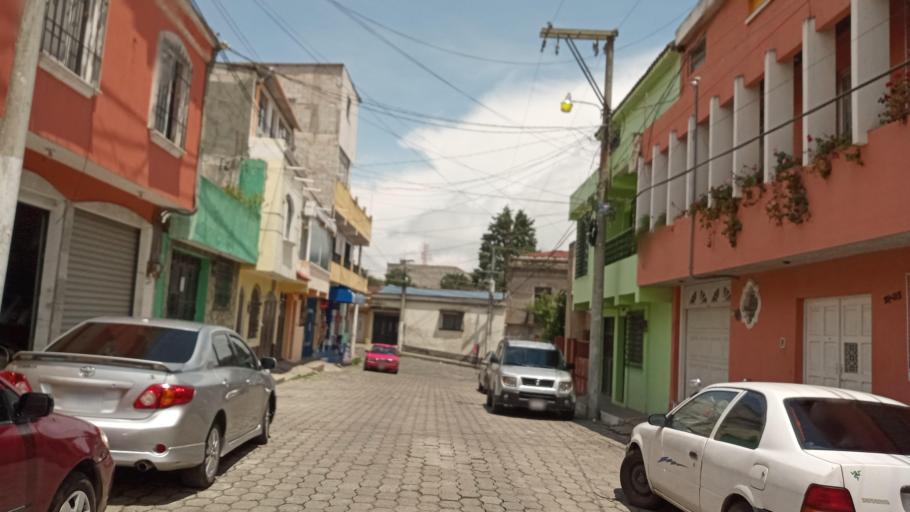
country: GT
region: Quetzaltenango
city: Quetzaltenango
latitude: 14.8418
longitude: -91.5156
